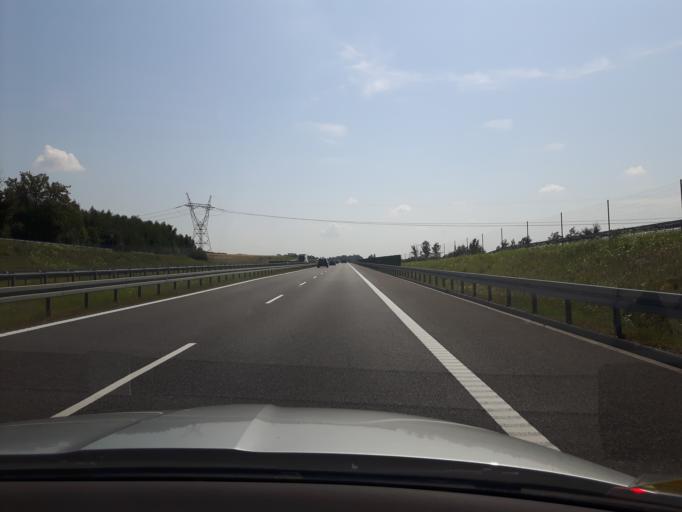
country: PL
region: Warmian-Masurian Voivodeship
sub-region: Powiat elblaski
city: Gronowo Gorne
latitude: 54.1216
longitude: 19.4673
